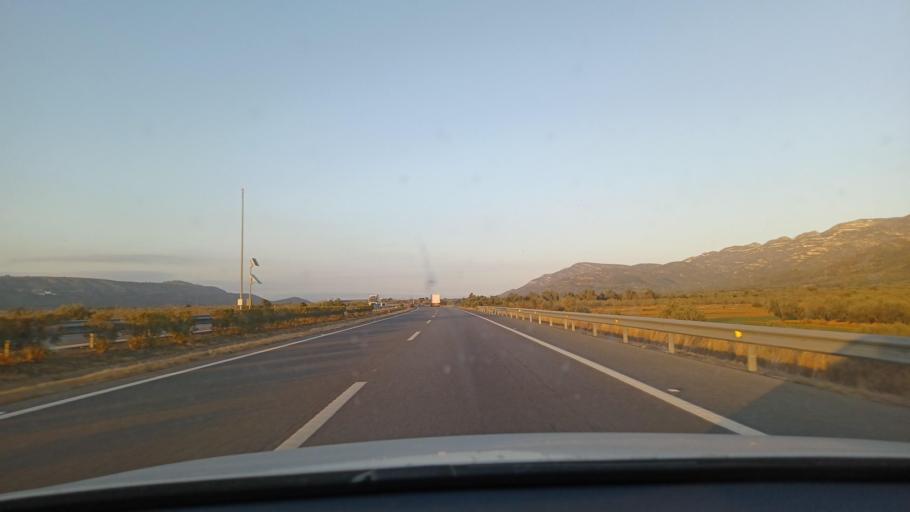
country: ES
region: Catalonia
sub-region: Provincia de Tarragona
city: Ulldecona
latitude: 40.5927
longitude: 0.4669
